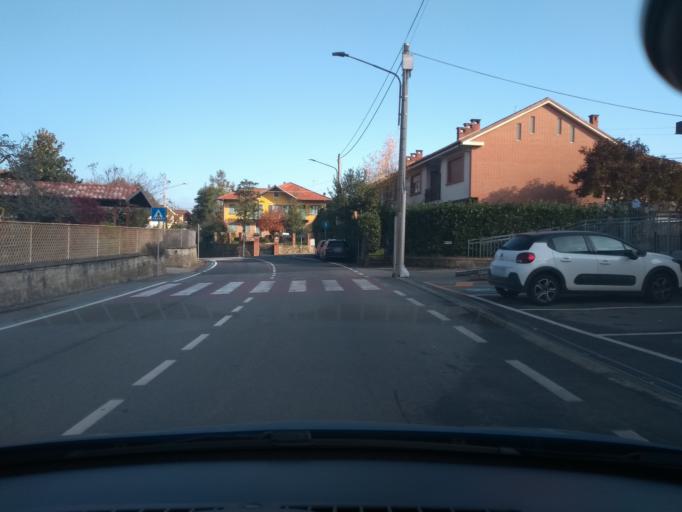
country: IT
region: Piedmont
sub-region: Provincia di Torino
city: Fiano
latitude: 45.2154
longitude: 7.5269
